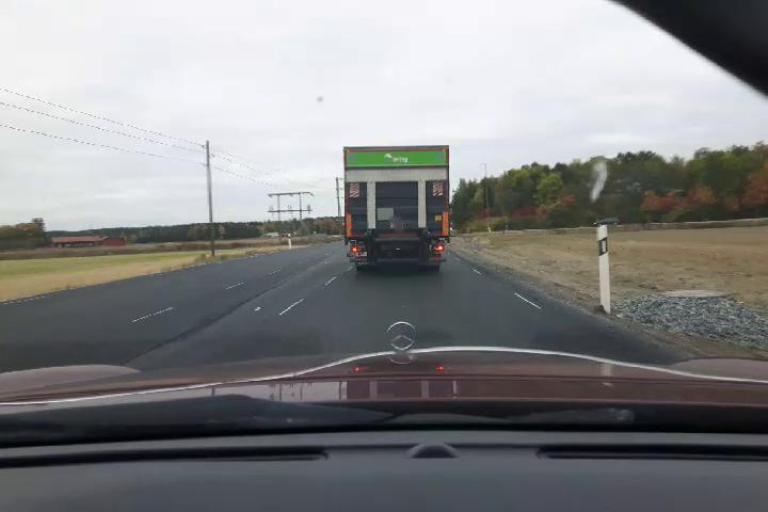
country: SE
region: Uppsala
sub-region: Enkopings Kommun
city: Enkoping
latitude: 59.6314
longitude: 17.0490
